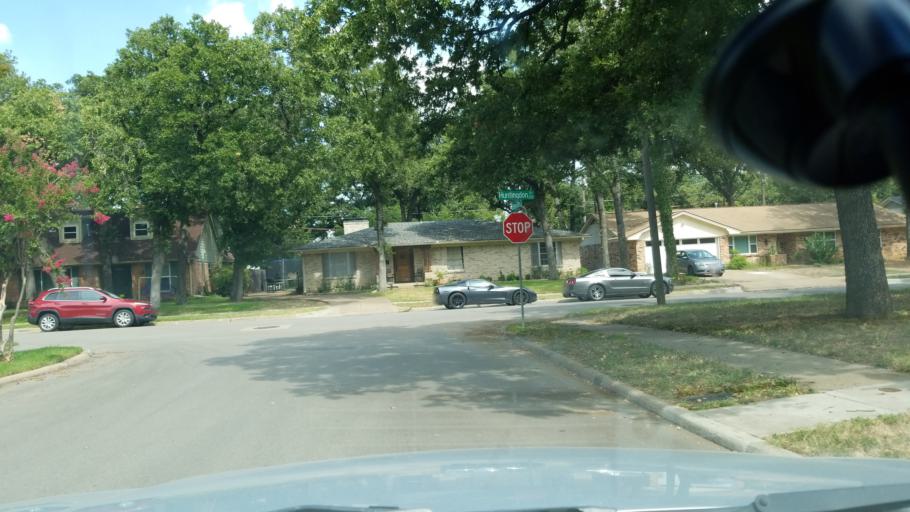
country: US
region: Texas
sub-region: Dallas County
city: Irving
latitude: 32.8176
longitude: -96.9798
